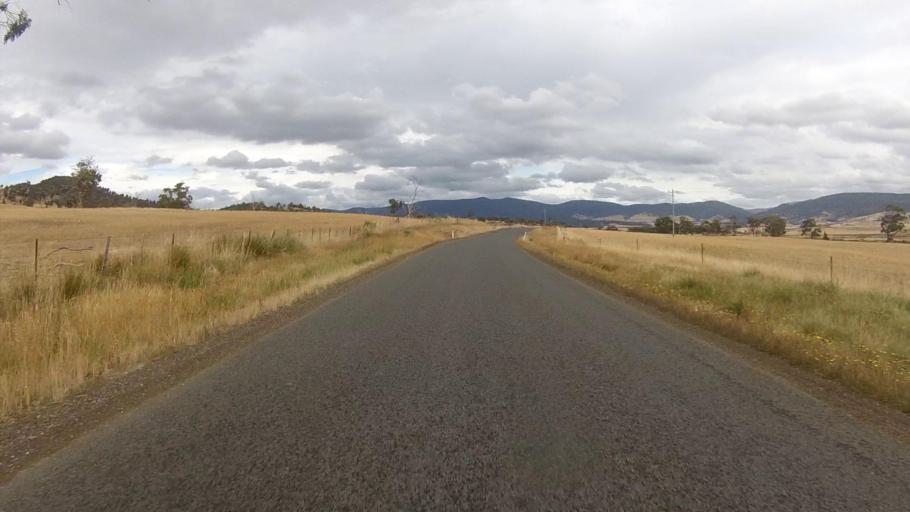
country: AU
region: Tasmania
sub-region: Northern Midlands
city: Evandale
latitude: -41.7993
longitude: 147.7491
